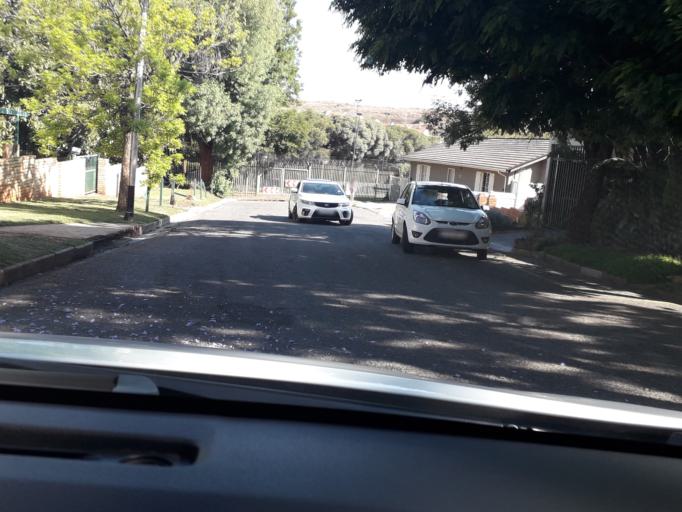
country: ZA
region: Gauteng
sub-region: City of Johannesburg Metropolitan Municipality
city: Johannesburg
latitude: -26.1774
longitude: 27.9945
